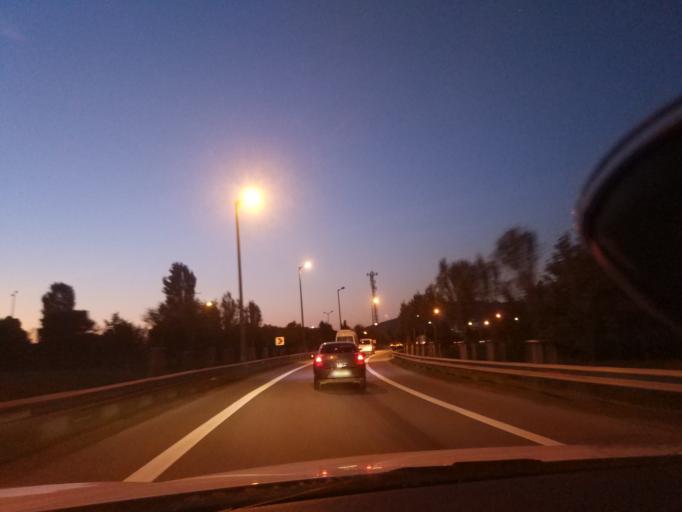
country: TR
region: Istanbul
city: Sultanbeyli
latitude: 40.9365
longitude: 29.3308
